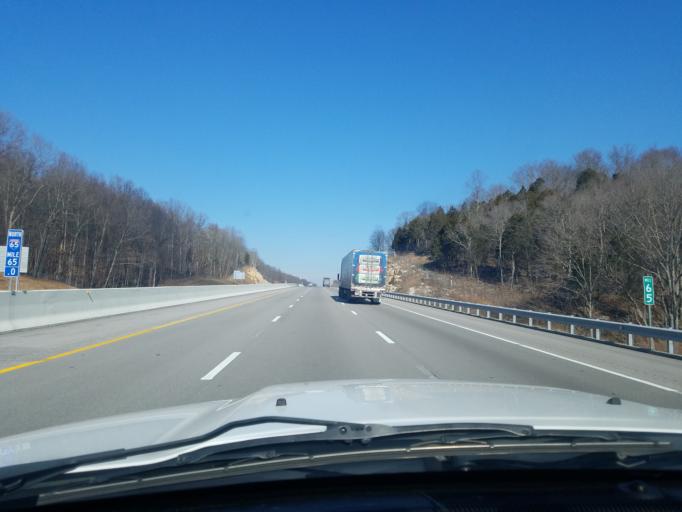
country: US
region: Kentucky
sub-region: Hart County
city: Munfordville
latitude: 37.3043
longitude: -85.9026
